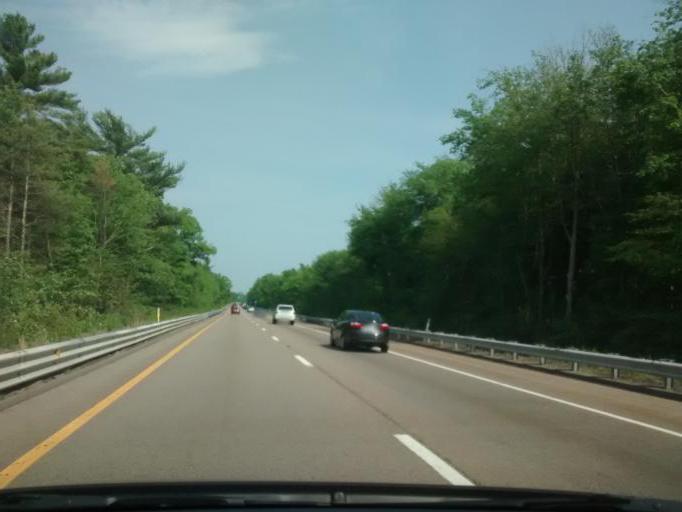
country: US
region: Massachusetts
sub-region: Plymouth County
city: West Wareham
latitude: 41.8105
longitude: -70.7836
